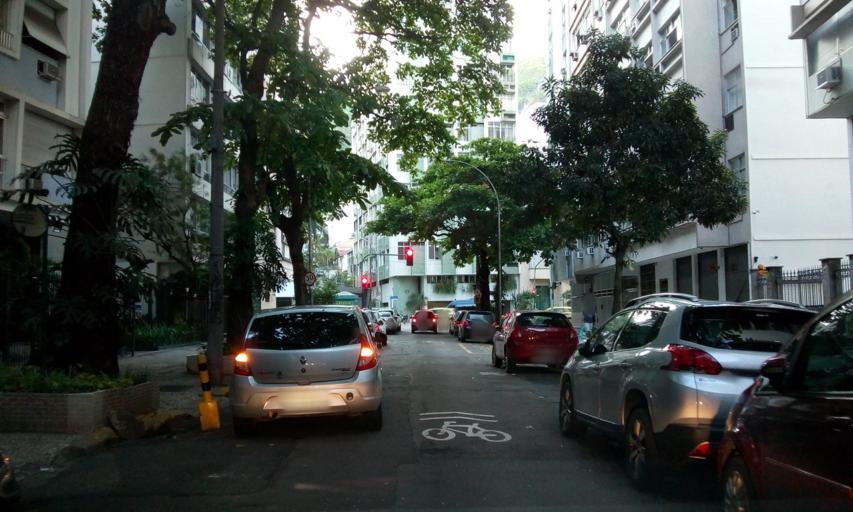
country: BR
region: Rio de Janeiro
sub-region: Rio De Janeiro
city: Rio de Janeiro
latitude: -22.9742
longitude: -43.1919
